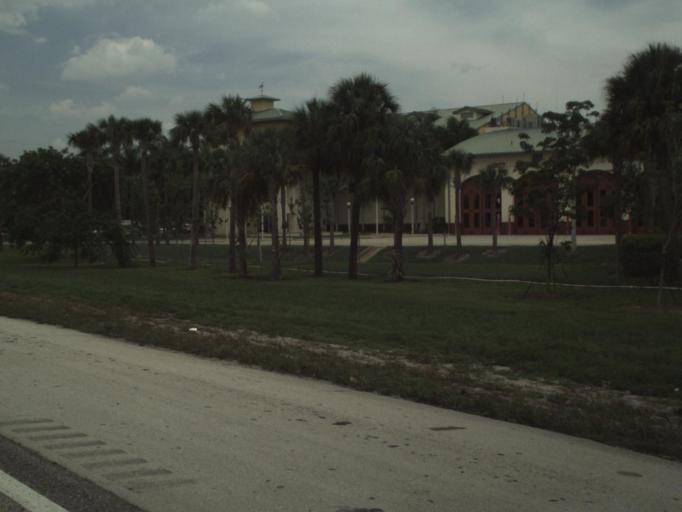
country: US
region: Florida
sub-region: Broward County
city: Tedder
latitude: 26.2981
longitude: -80.1213
